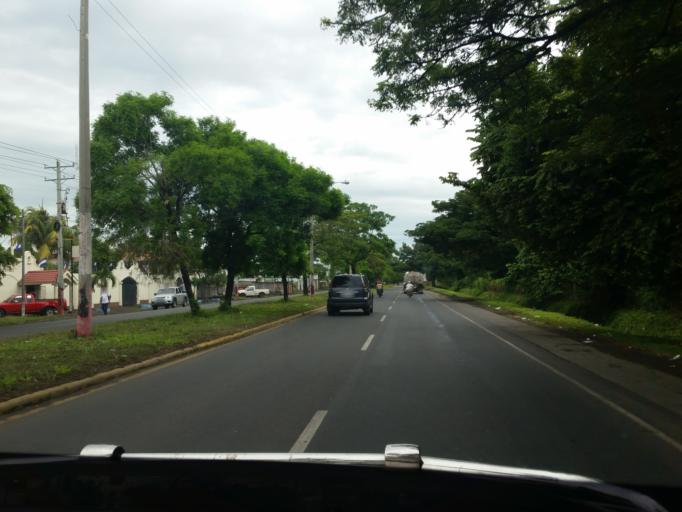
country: NI
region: Managua
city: Tipitapa
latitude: 12.1506
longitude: -86.1542
